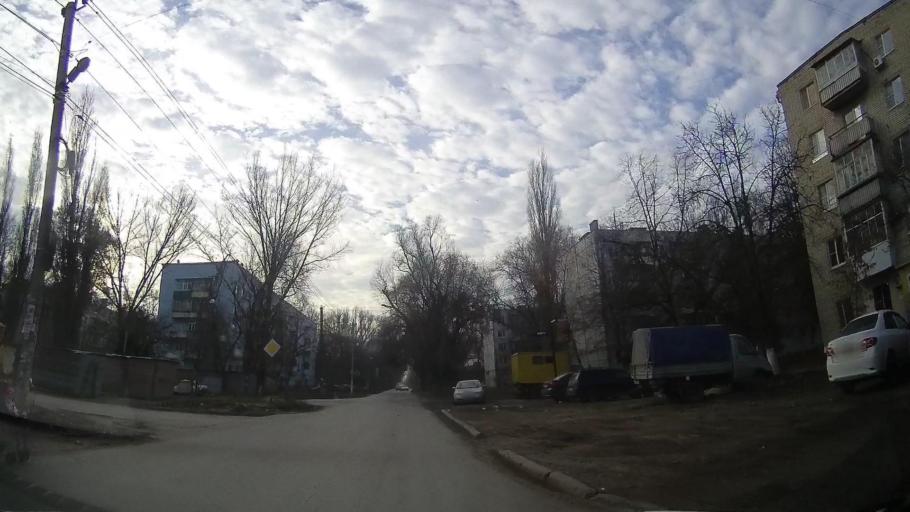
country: RU
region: Rostov
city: Bataysk
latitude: 47.1261
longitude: 39.7788
